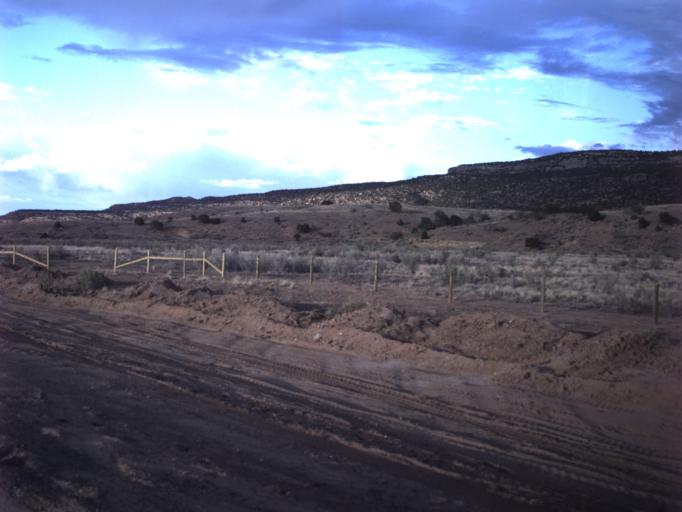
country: US
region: Utah
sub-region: San Juan County
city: Monticello
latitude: 38.0440
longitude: -109.3427
